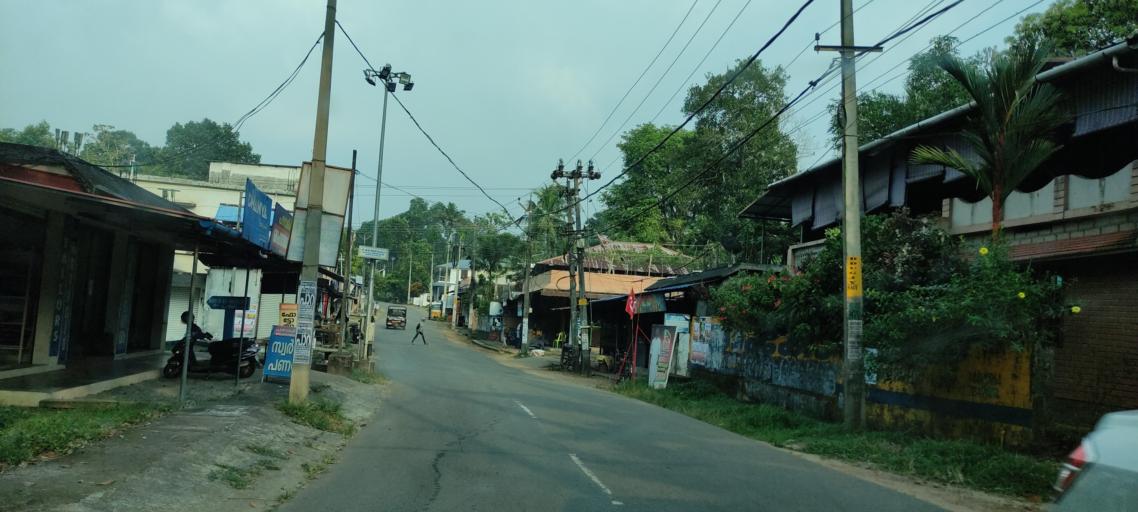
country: IN
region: Kerala
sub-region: Pattanamtitta
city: Adur
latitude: 9.0890
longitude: 76.7441
